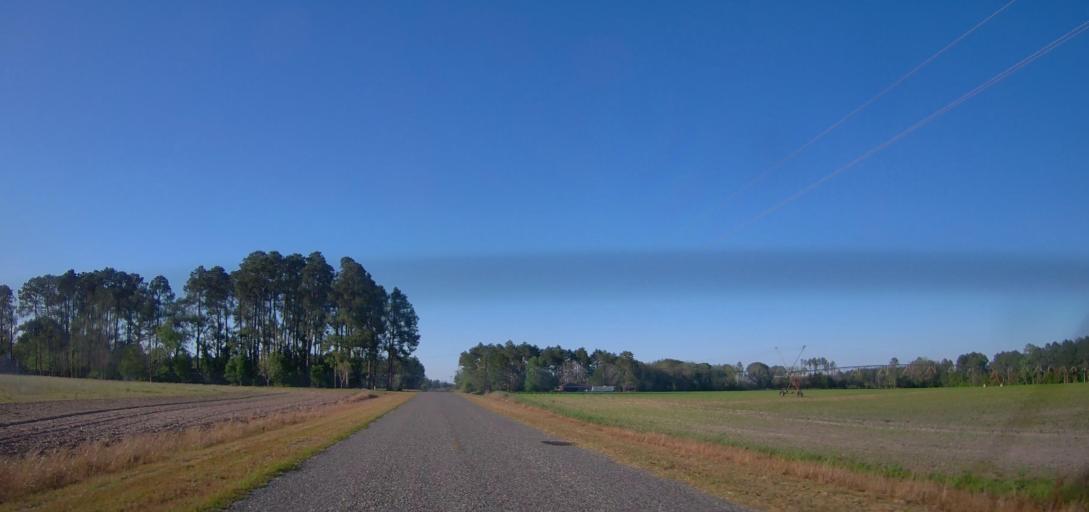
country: US
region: Georgia
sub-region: Ben Hill County
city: Fitzgerald
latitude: 31.6673
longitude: -83.1468
